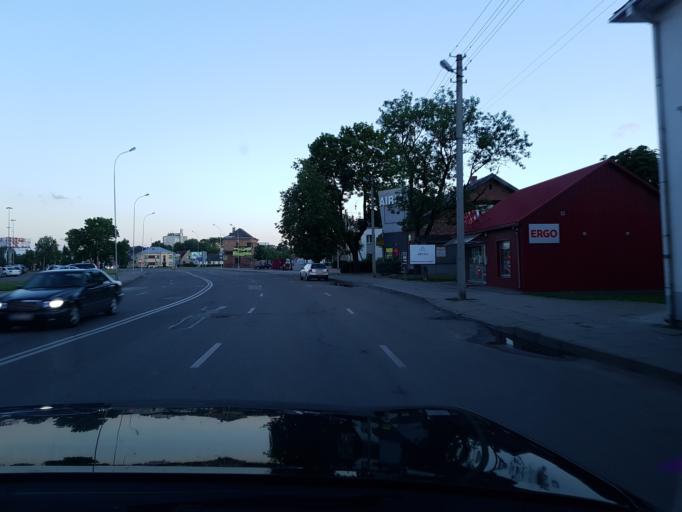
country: LT
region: Marijampoles apskritis
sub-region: Marijampole Municipality
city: Marijampole
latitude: 54.5629
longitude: 23.3541
